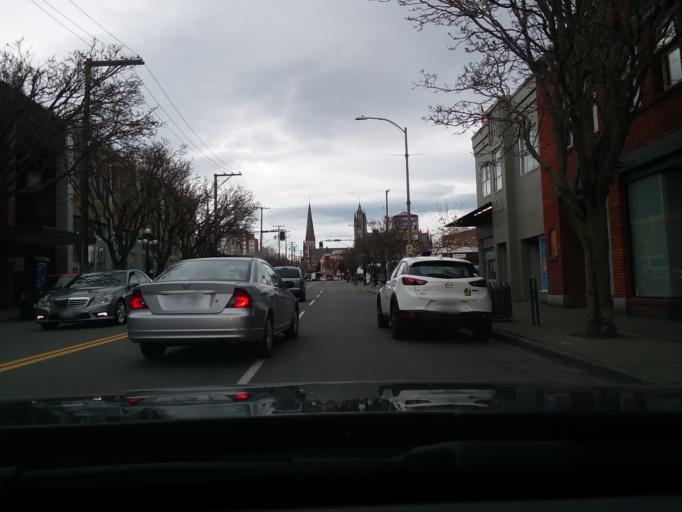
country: CA
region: British Columbia
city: Victoria
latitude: 48.4250
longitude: -123.3594
